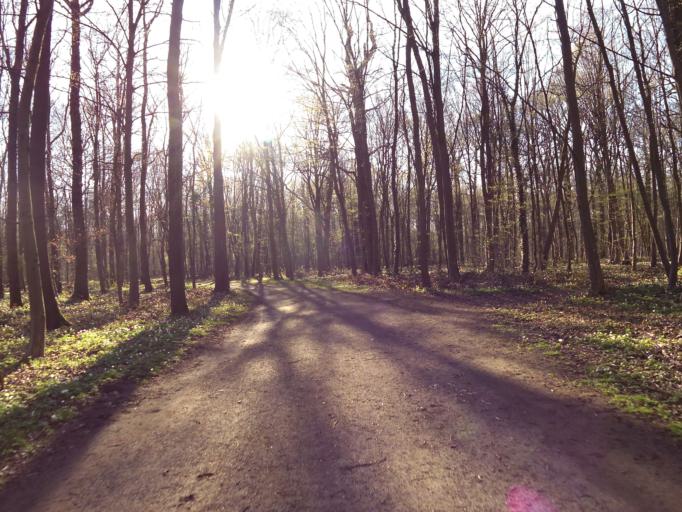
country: DE
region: Lower Saxony
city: Hannover
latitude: 52.3833
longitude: 9.7891
